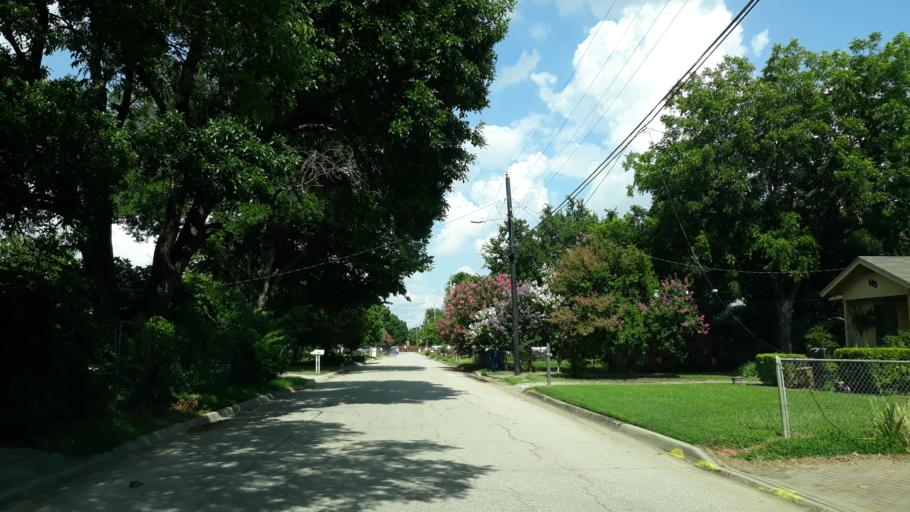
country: US
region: Texas
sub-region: Dallas County
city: Coppell
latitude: 32.9604
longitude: -97.0050
